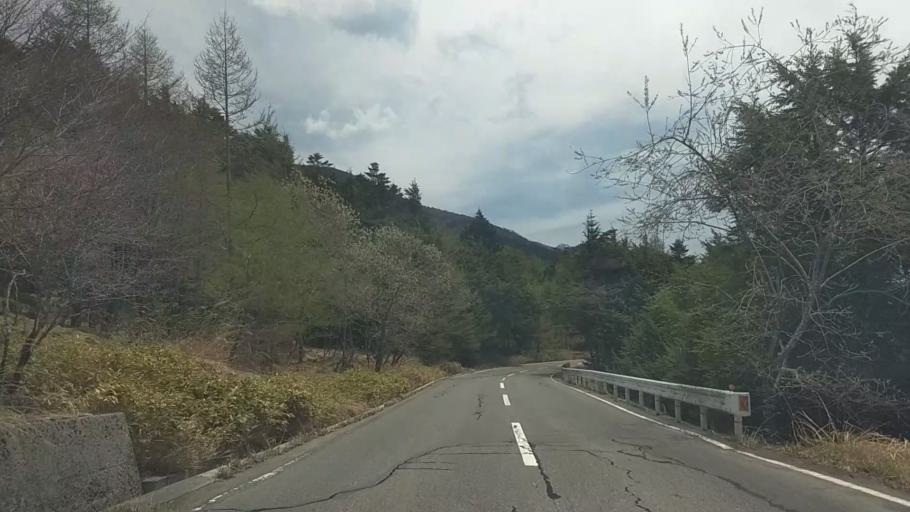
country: JP
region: Nagano
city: Chino
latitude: 36.0540
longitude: 138.3196
